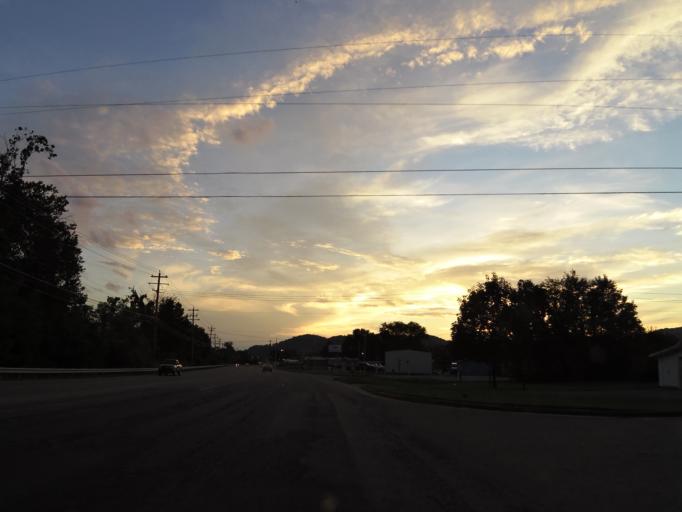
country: US
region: Tennessee
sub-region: Carter County
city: Hunter
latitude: 36.3695
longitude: -82.1654
